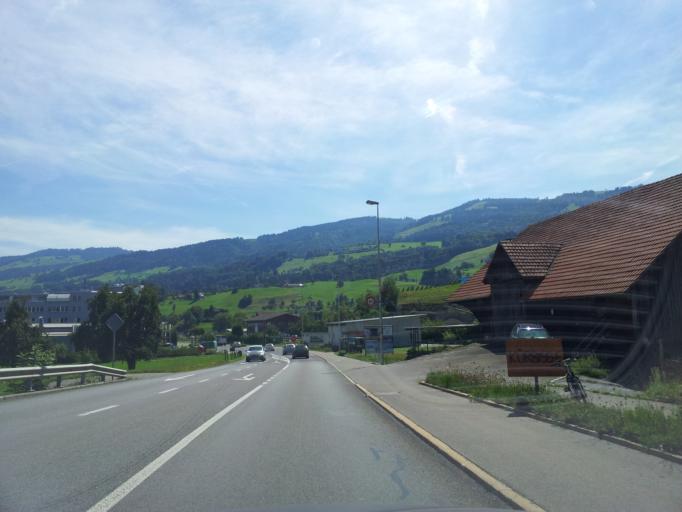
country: CH
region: Schwyz
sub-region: Bezirk March
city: Altendorf
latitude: 47.1998
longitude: 8.8108
